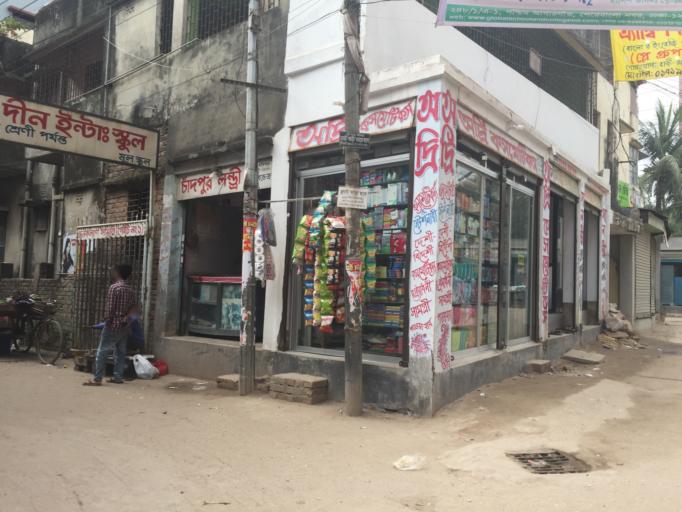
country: BD
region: Dhaka
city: Azimpur
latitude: 23.7843
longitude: 90.3636
